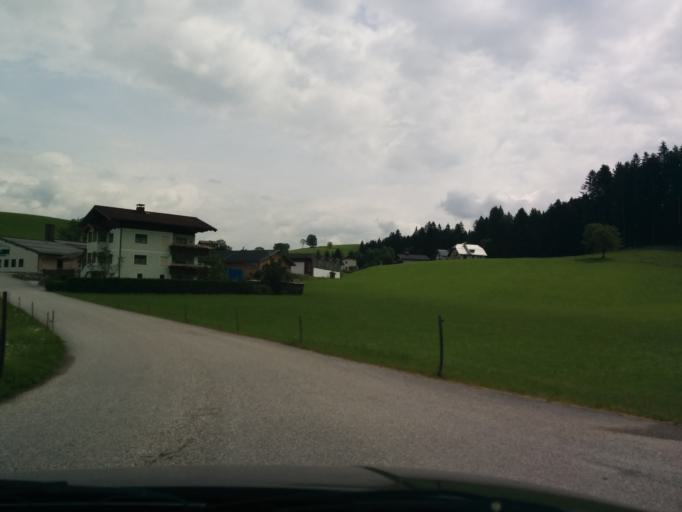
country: AT
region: Salzburg
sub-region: Politischer Bezirk Hallein
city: Abtenau
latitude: 47.5580
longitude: 13.3526
